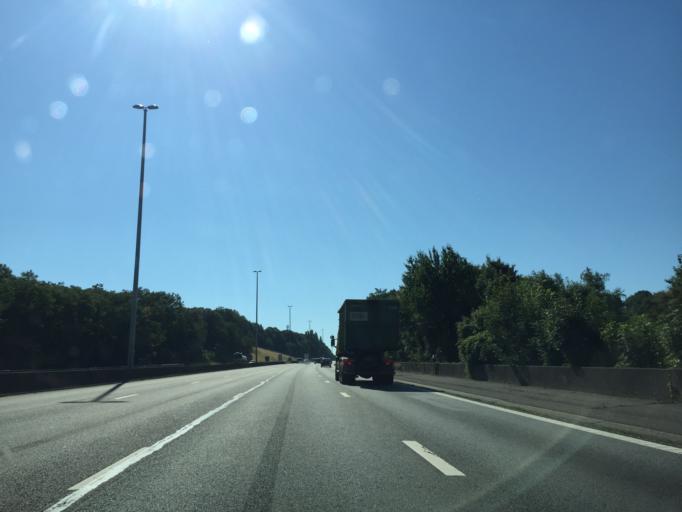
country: BE
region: Wallonia
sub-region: Province de Liege
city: Blegny
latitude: 50.6734
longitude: 5.6808
